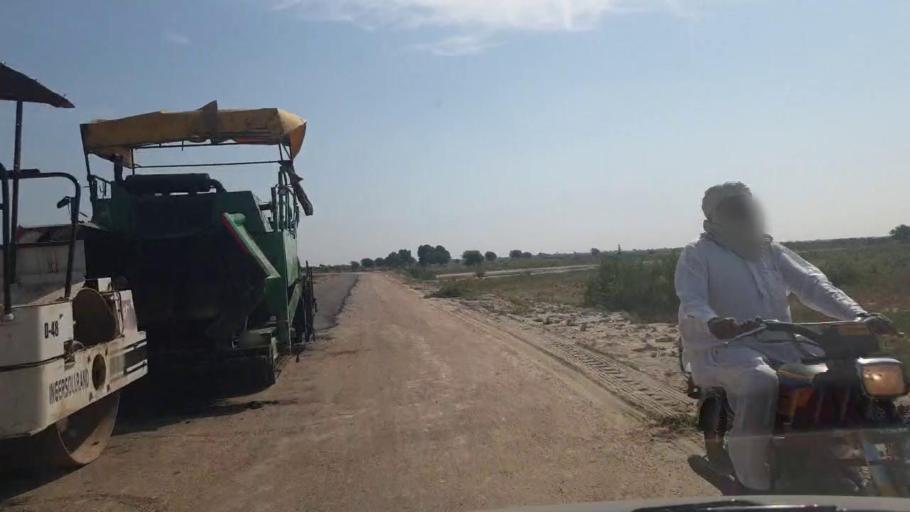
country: PK
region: Sindh
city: Digri
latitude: 24.9732
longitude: 69.1237
